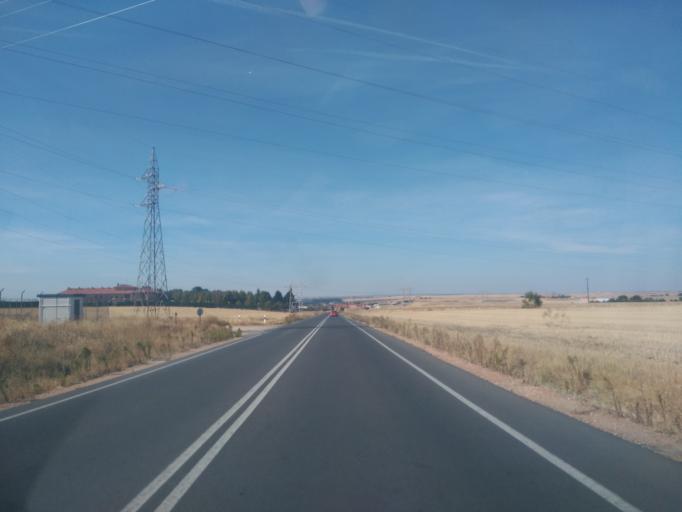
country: ES
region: Castille and Leon
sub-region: Provincia de Salamanca
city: Villamayor
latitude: 40.9902
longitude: -5.6885
